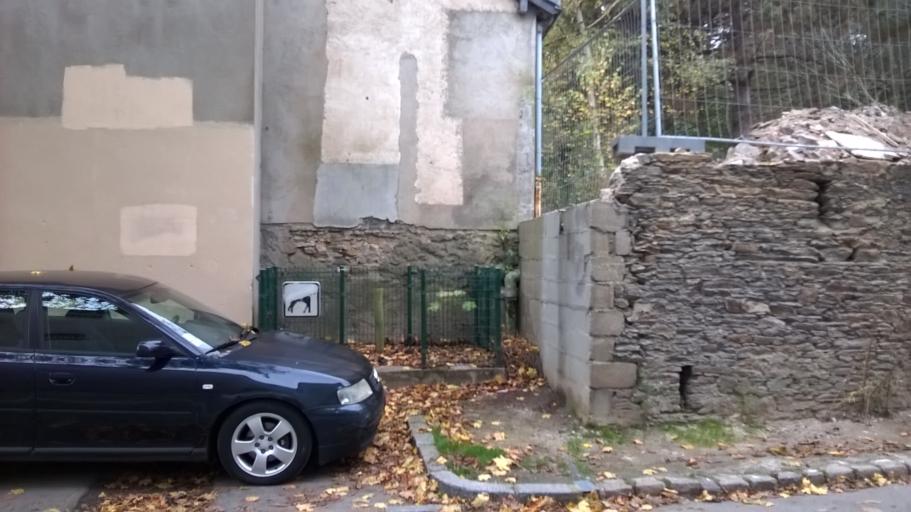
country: FR
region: Pays de la Loire
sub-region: Departement de la Loire-Atlantique
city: Nantes
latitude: 47.2253
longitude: -1.5611
